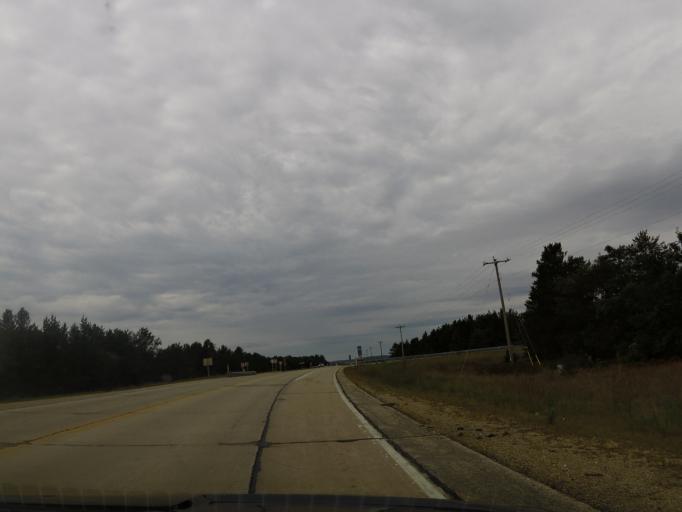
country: US
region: Wisconsin
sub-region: Monroe County
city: Sparta
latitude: 43.9411
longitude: -90.7610
